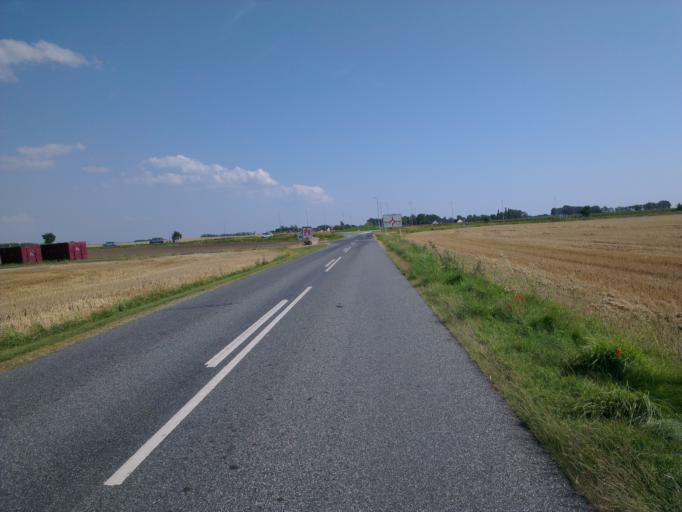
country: DK
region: Capital Region
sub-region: Frederikssund Kommune
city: Skibby
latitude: 55.7911
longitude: 11.9738
